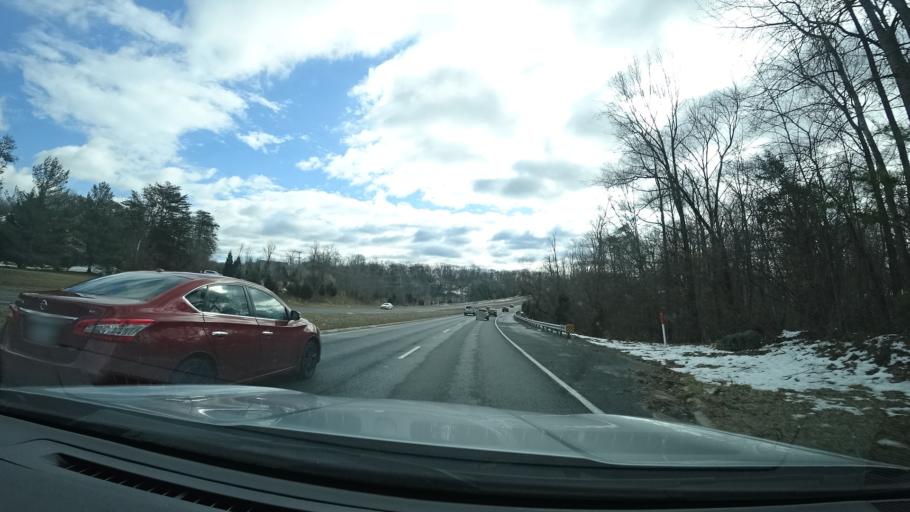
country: US
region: Virginia
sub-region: Fairfax County
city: Dranesville
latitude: 38.9889
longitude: -77.3612
